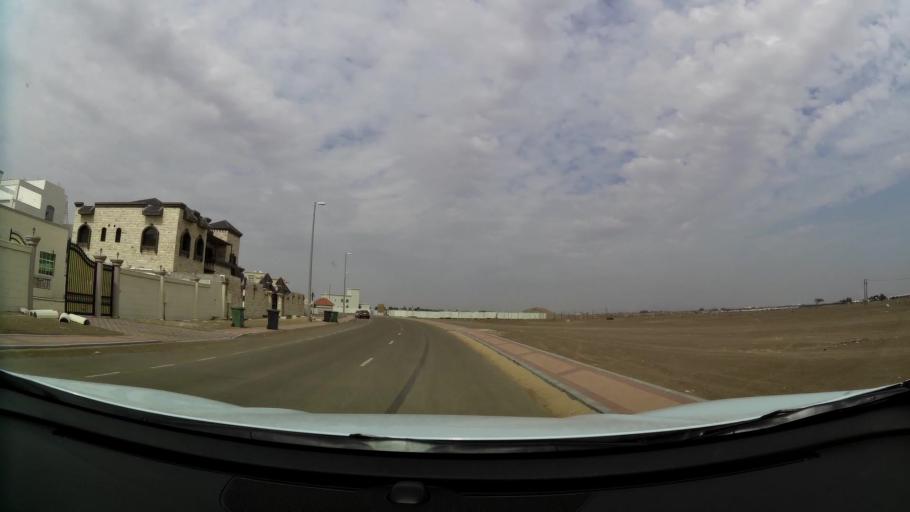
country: AE
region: Abu Dhabi
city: Al Ain
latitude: 24.1887
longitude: 55.8189
